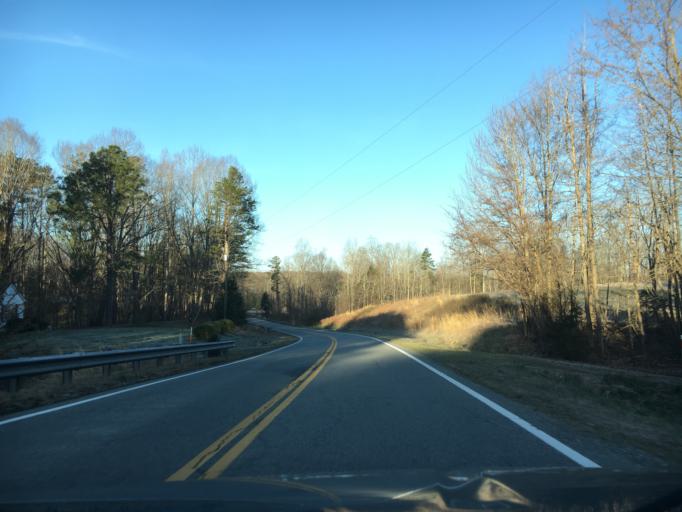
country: US
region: Virginia
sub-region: Halifax County
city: Halifax
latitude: 36.7615
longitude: -78.9004
